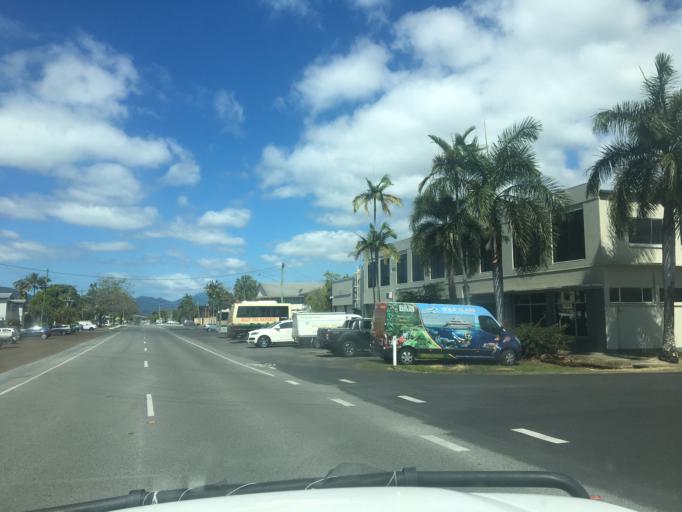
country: AU
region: Queensland
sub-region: Cairns
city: Cairns
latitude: -16.9247
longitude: 145.7670
